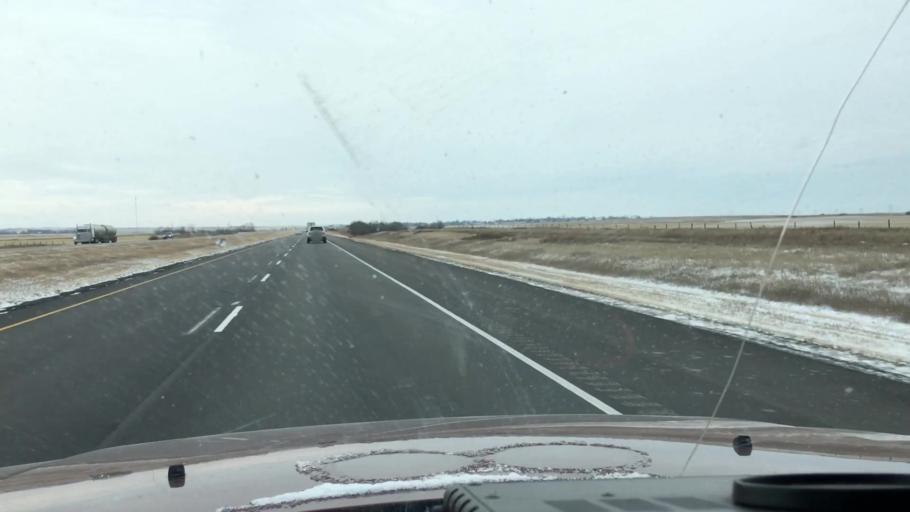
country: CA
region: Saskatchewan
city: Saskatoon
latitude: 51.8367
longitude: -106.5036
